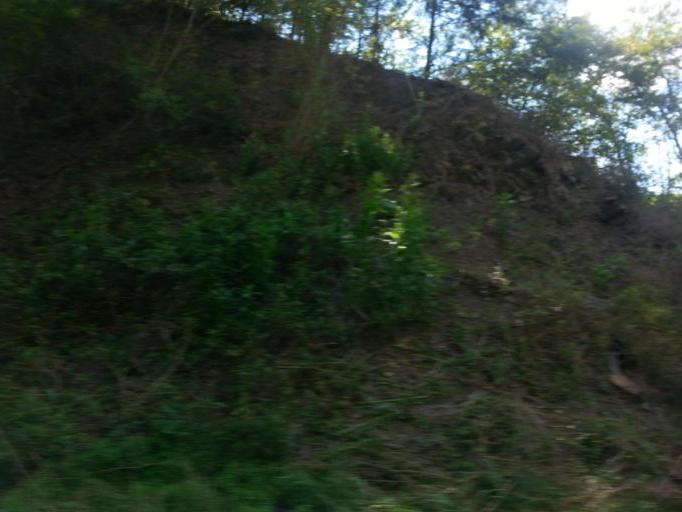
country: US
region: Virginia
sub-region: Washington County
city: Abingdon
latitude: 36.6771
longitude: -81.9742
